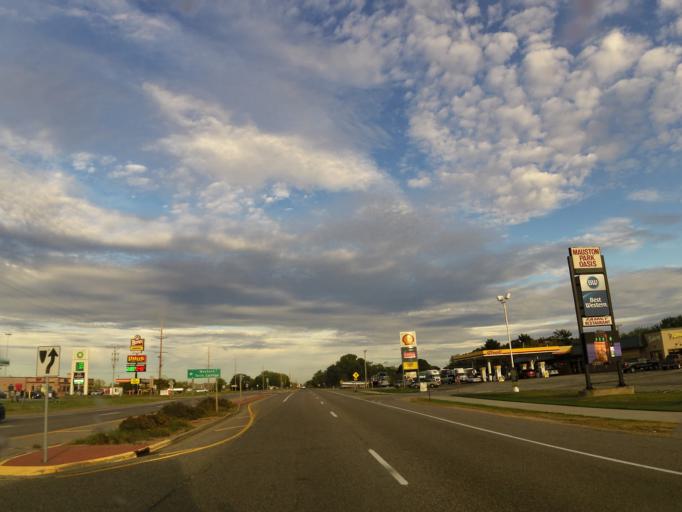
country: US
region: Wisconsin
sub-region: Juneau County
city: Mauston
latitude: 43.7963
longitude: -90.0533
